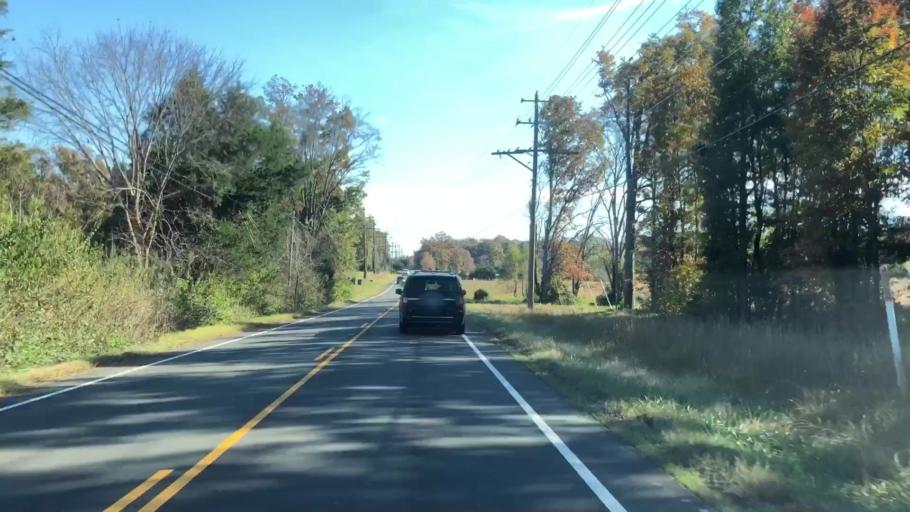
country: US
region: Virginia
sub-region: Prince William County
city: Linton Hall
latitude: 38.7448
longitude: -77.6075
